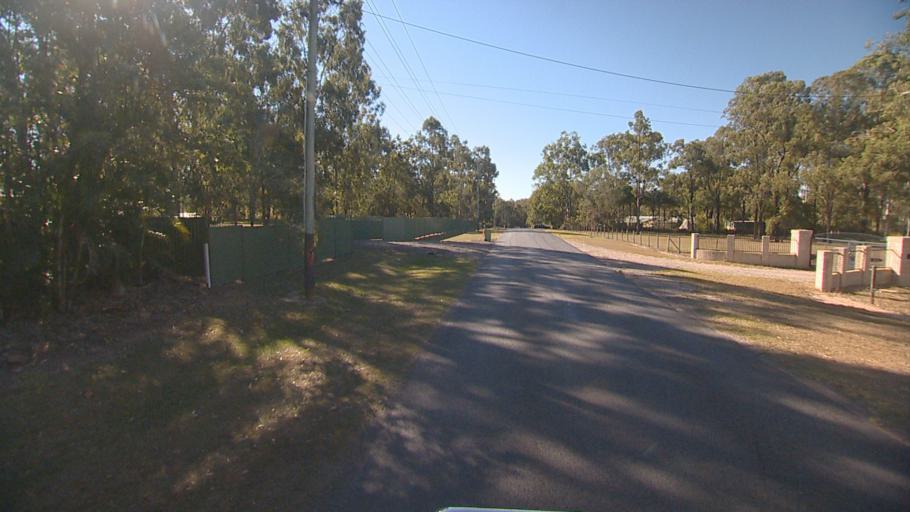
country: AU
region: Queensland
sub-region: Logan
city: Park Ridge South
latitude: -27.7265
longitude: 153.0202
